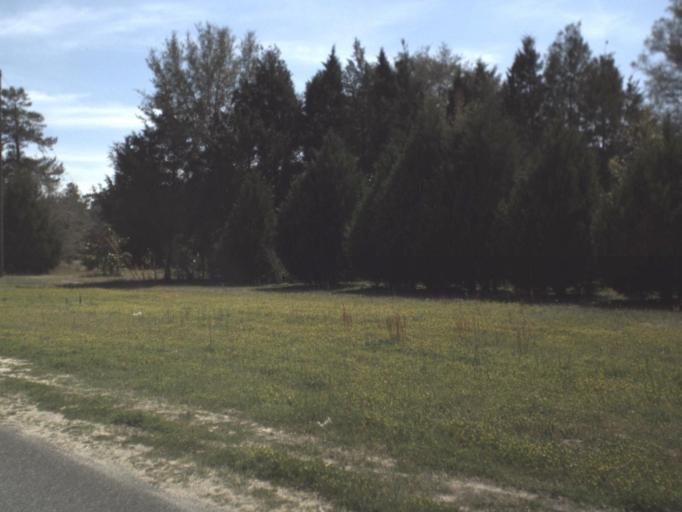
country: US
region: Florida
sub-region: Bay County
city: Lynn Haven
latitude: 30.3795
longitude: -85.6802
